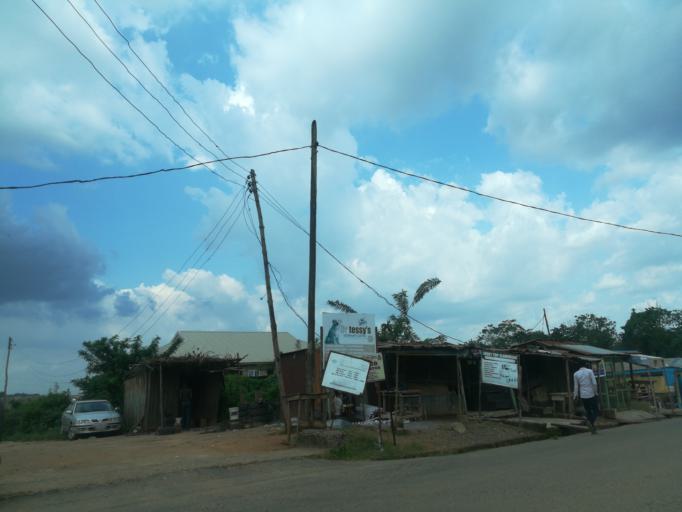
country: NG
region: Oyo
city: Ibadan
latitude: 7.4019
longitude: 3.8361
